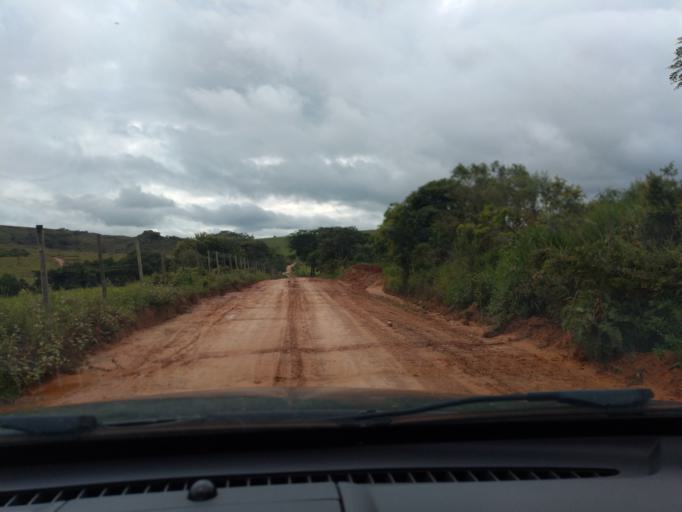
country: BR
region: Minas Gerais
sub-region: Lavras
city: Lavras
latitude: -21.5115
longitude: -44.9278
